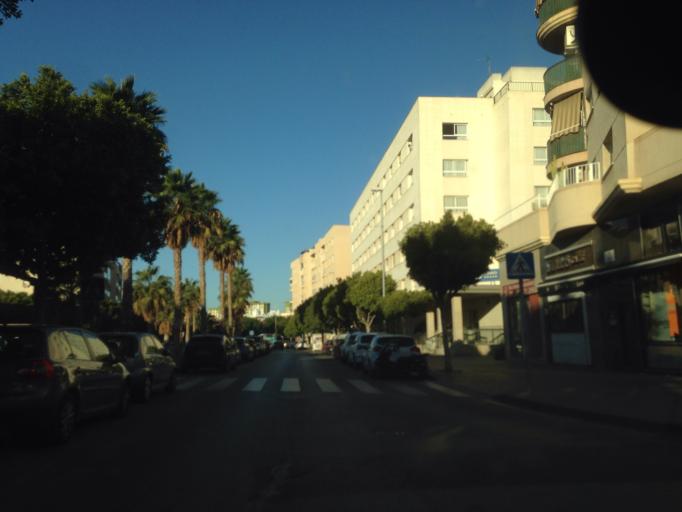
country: ES
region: Andalusia
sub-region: Provincia de Malaga
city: Malaga
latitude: 36.7215
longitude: -4.4777
